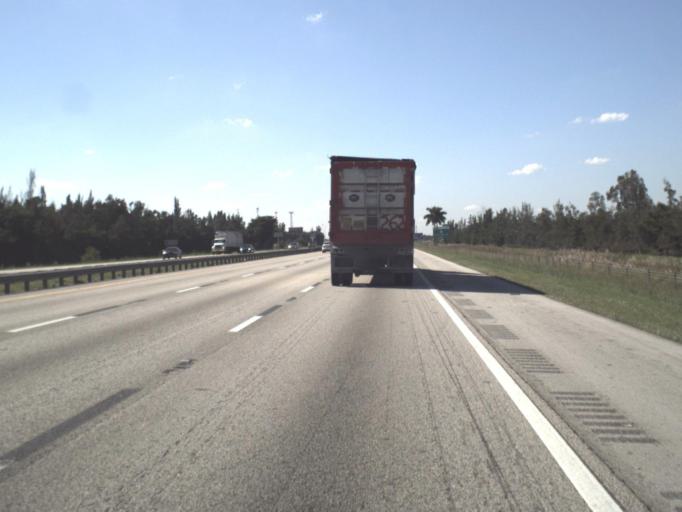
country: US
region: Florida
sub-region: Miami-Dade County
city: Palm Springs North
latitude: 25.9176
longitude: -80.3794
